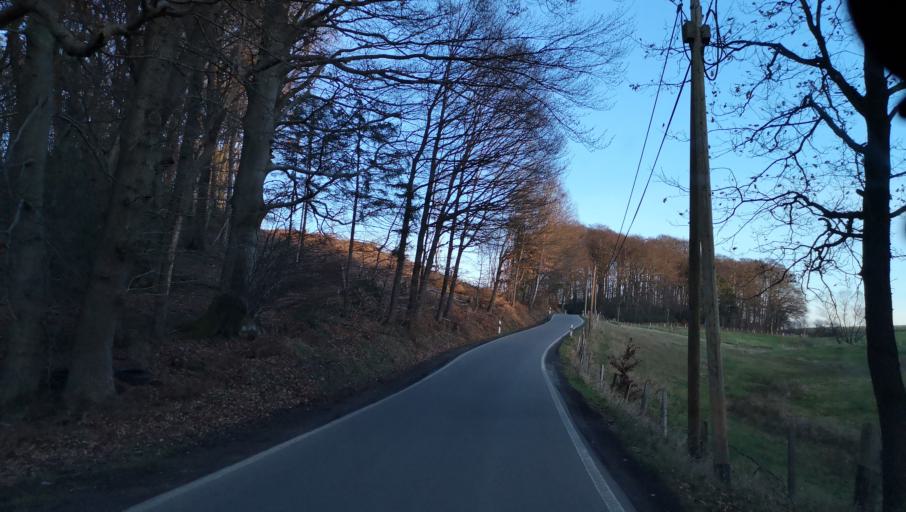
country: DE
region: North Rhine-Westphalia
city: Huckeswagen
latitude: 51.1749
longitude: 7.3526
